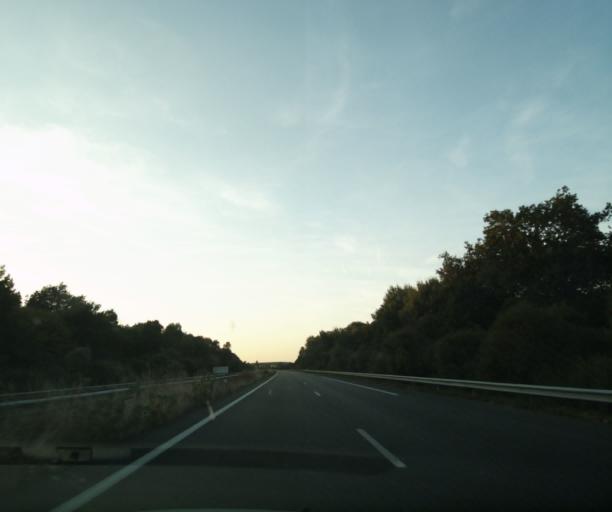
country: FR
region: Aquitaine
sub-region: Departement du Lot-et-Garonne
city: Fourques-sur-Garonne
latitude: 44.4174
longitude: 0.1752
